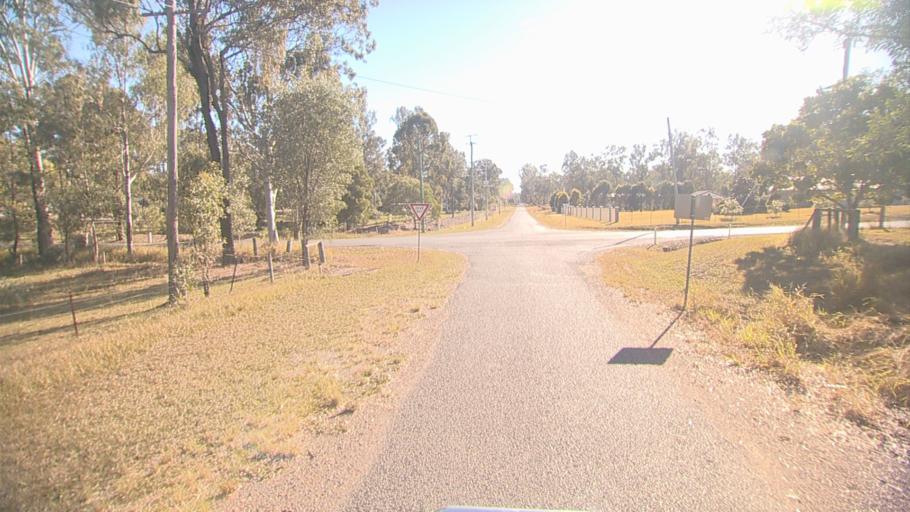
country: AU
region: Queensland
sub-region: Logan
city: North Maclean
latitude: -27.7587
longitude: 153.0331
